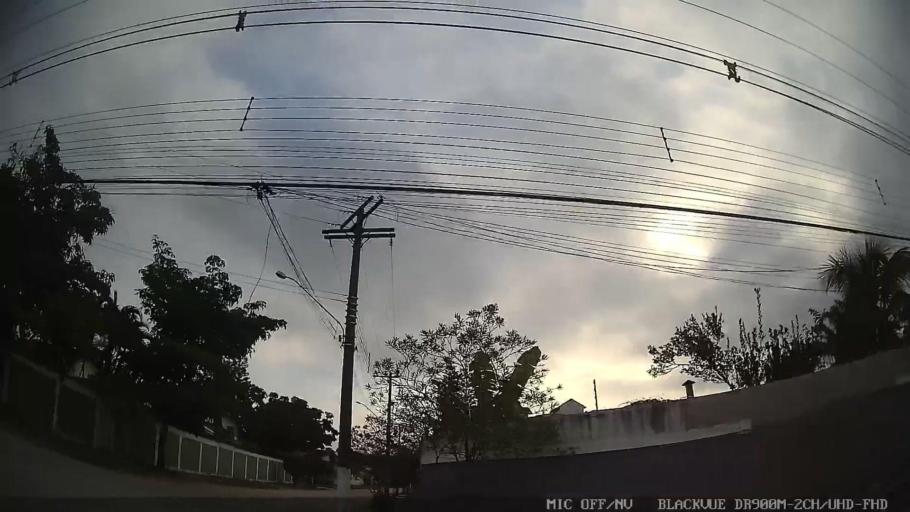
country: BR
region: Sao Paulo
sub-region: Guaruja
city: Guaruja
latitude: -23.9705
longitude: -46.2110
